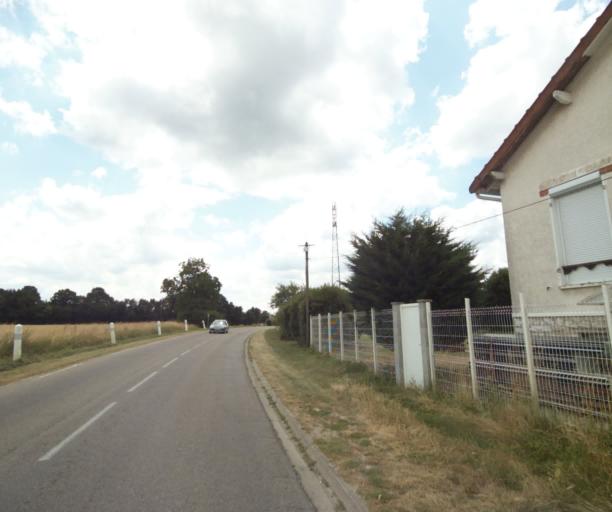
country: FR
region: Ile-de-France
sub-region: Departement de Seine-et-Marne
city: Vulaines-sur-Seine
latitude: 48.4353
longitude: 2.7711
